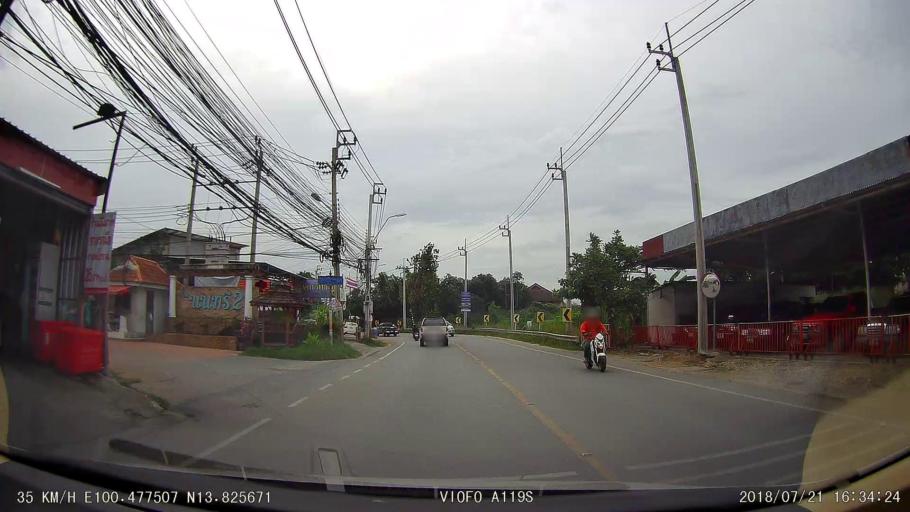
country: TH
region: Nonthaburi
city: Bang Kruai
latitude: 13.8257
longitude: 100.4775
